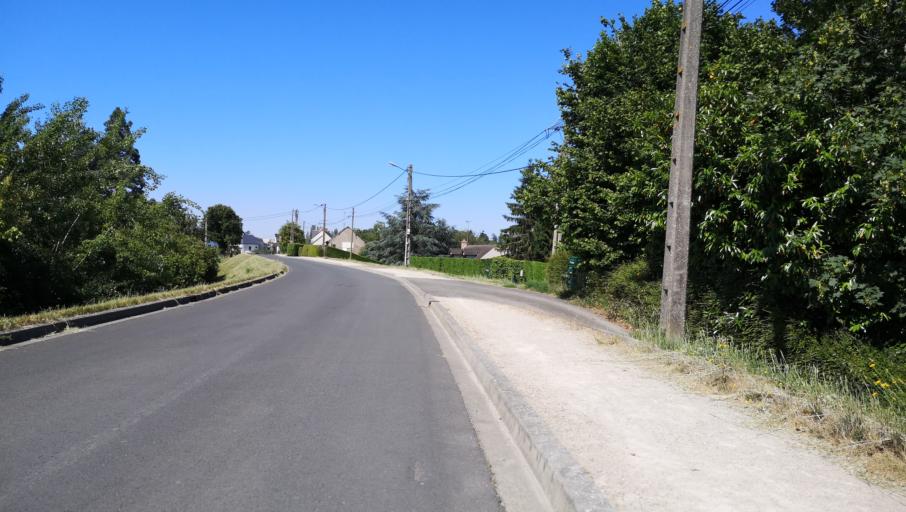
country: FR
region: Centre
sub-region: Departement du Loiret
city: Saint-Jean-le-Blanc
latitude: 47.8932
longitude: 1.9310
